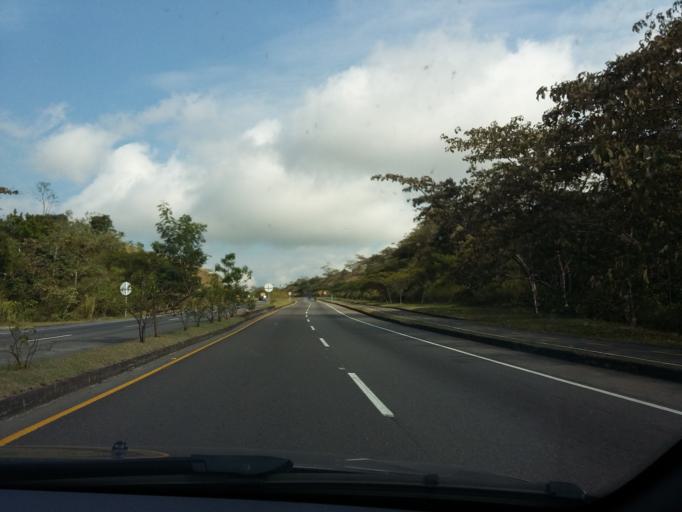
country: CO
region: Tolima
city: Ibague
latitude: 4.3506
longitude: -75.1086
